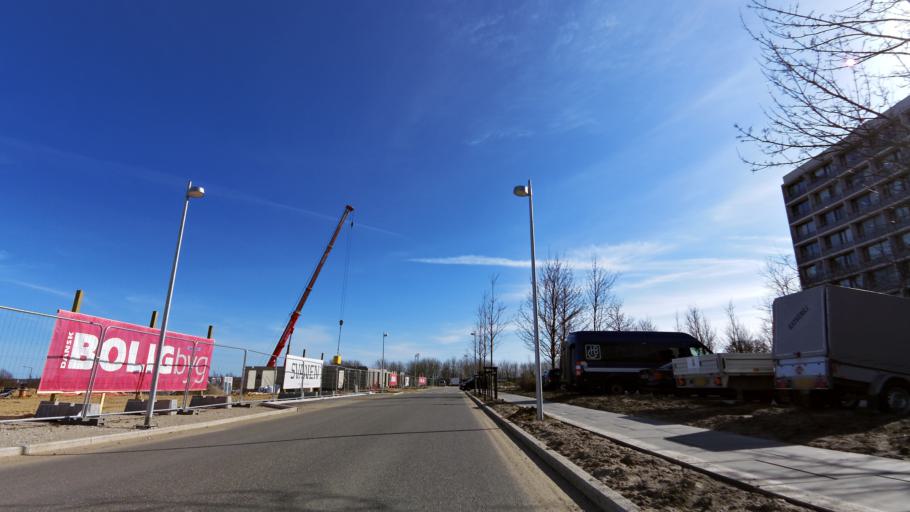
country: DK
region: Central Jutland
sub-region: Arhus Kommune
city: Stavtrup
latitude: 56.1570
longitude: 10.1405
